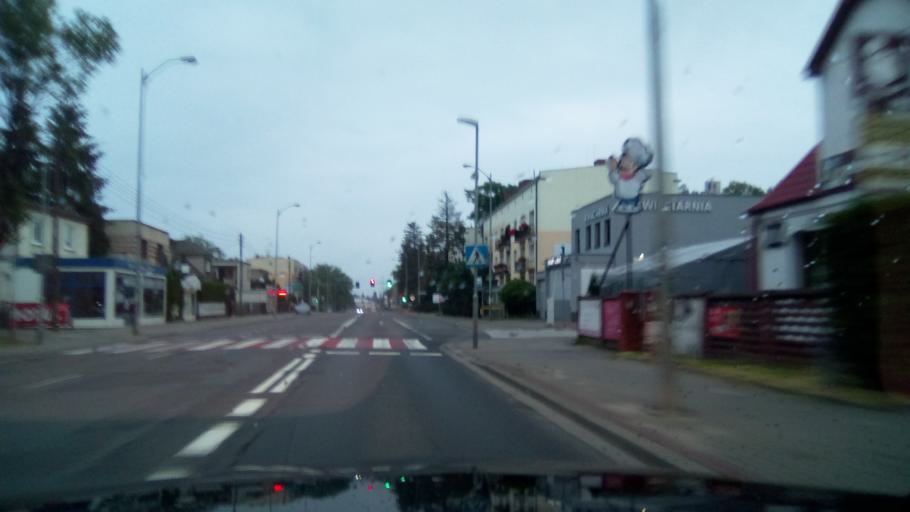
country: PL
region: Greater Poland Voivodeship
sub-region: Powiat poznanski
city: Swarzedz
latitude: 52.4113
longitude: 17.0848
